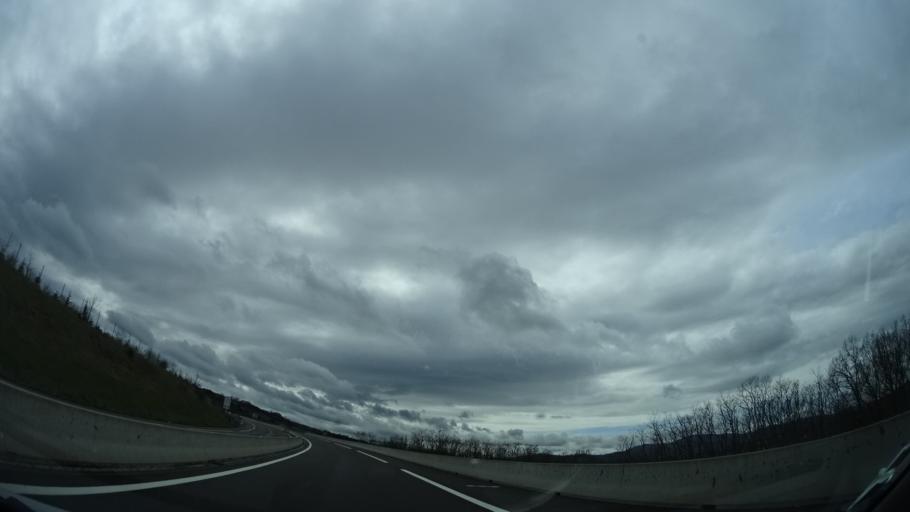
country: FR
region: Rhone-Alpes
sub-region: Departement du Rhone
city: Saint-Germain-Nuelles
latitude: 45.8452
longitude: 4.6407
